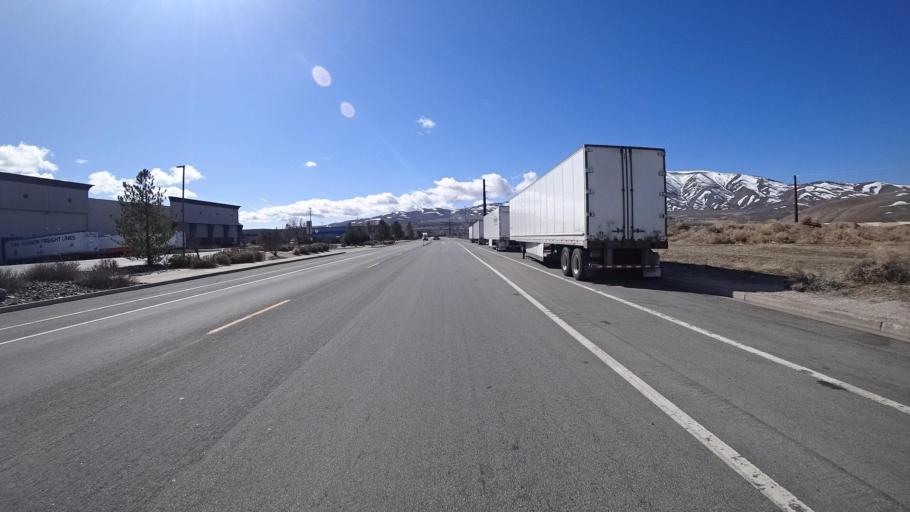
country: US
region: Nevada
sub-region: Washoe County
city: Lemmon Valley
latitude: 39.6440
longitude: -119.8972
